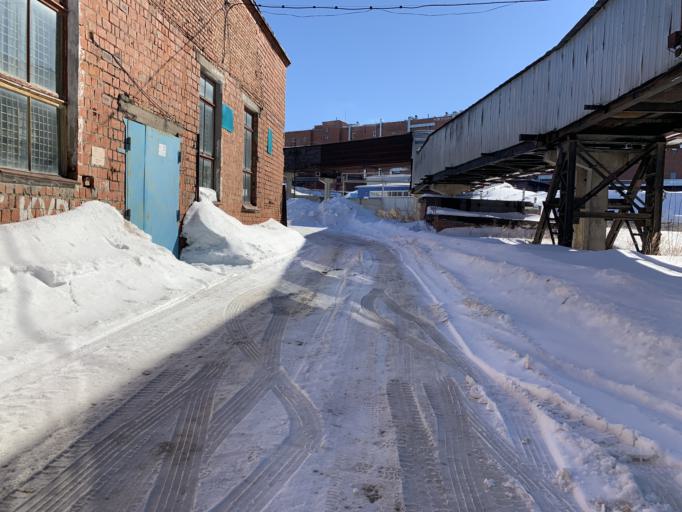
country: RU
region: Chuvashia
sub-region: Cheboksarskiy Rayon
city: Cheboksary
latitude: 56.1395
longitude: 47.2783
